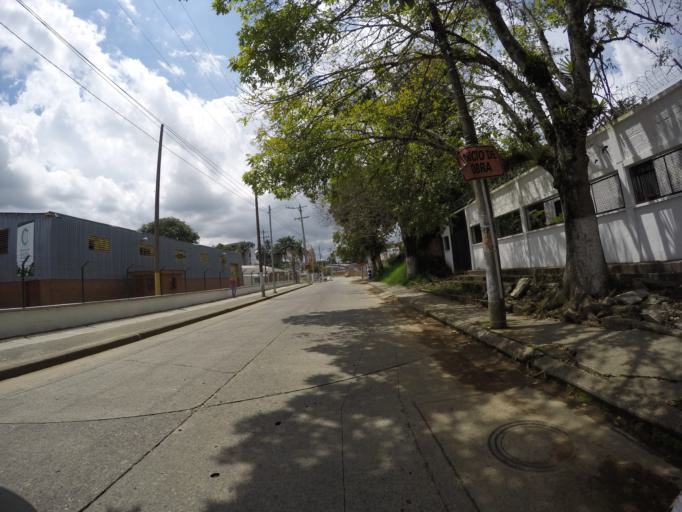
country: CO
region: Quindio
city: Quimbaya
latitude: 4.6206
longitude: -75.7668
